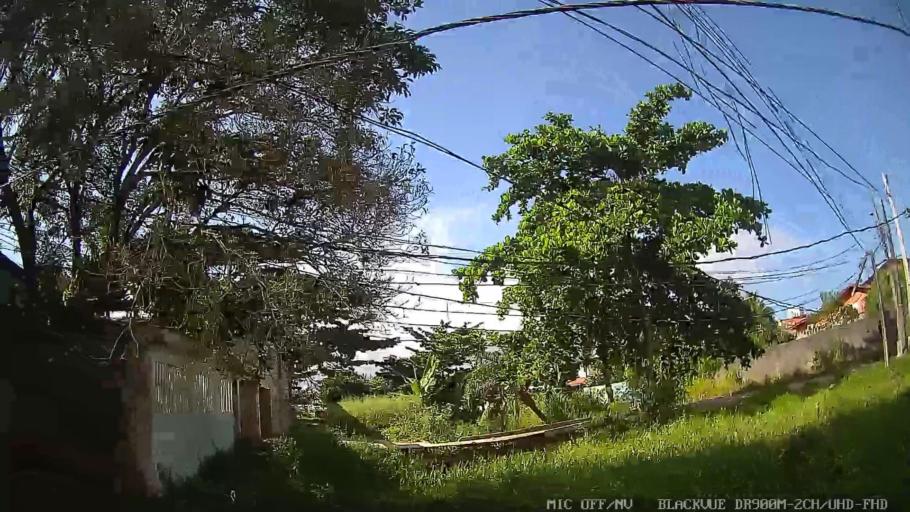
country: BR
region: Sao Paulo
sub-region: Peruibe
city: Peruibe
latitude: -24.2712
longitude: -46.9332
